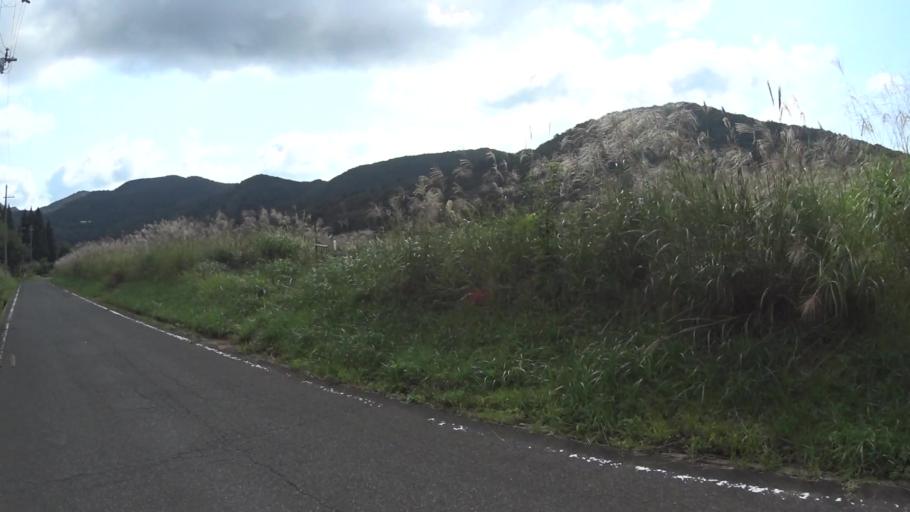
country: JP
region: Kyoto
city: Miyazu
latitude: 35.6556
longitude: 135.1818
